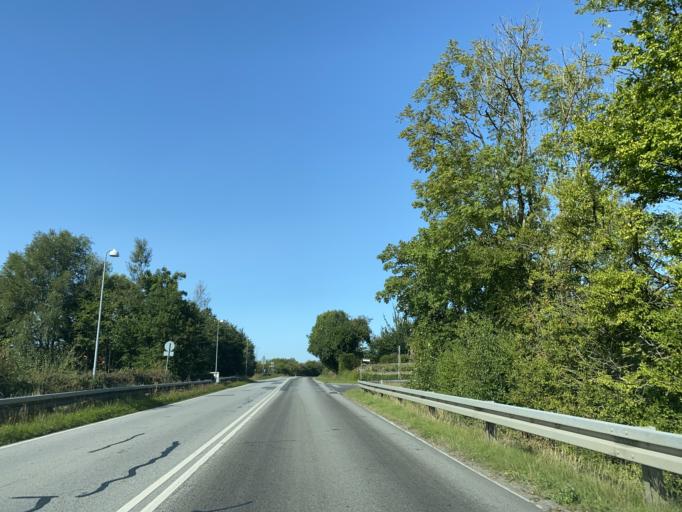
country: DK
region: South Denmark
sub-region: Aabenraa Kommune
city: Aabenraa
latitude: 55.0620
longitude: 9.3849
